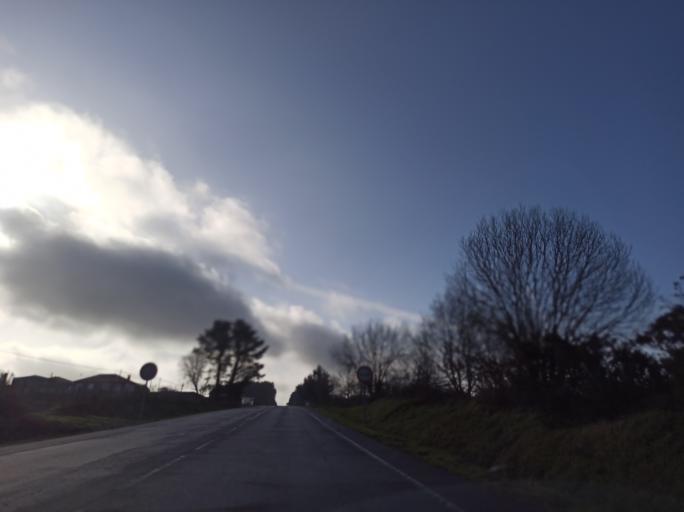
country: ES
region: Galicia
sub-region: Provincia da Coruna
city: Curtis
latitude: 43.1066
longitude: -8.0236
